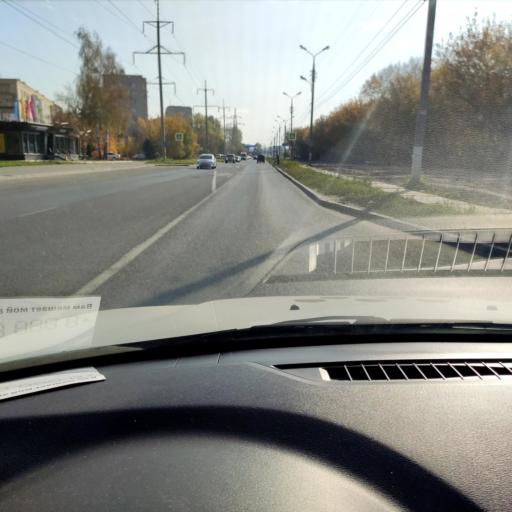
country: RU
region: Samara
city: Tol'yatti
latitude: 53.5280
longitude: 49.3961
